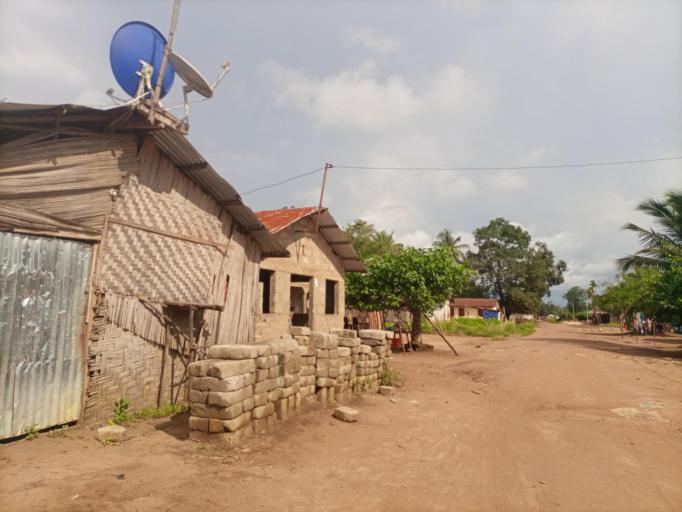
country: SL
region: Northern Province
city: Masoyila
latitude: 8.6171
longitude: -13.1715
